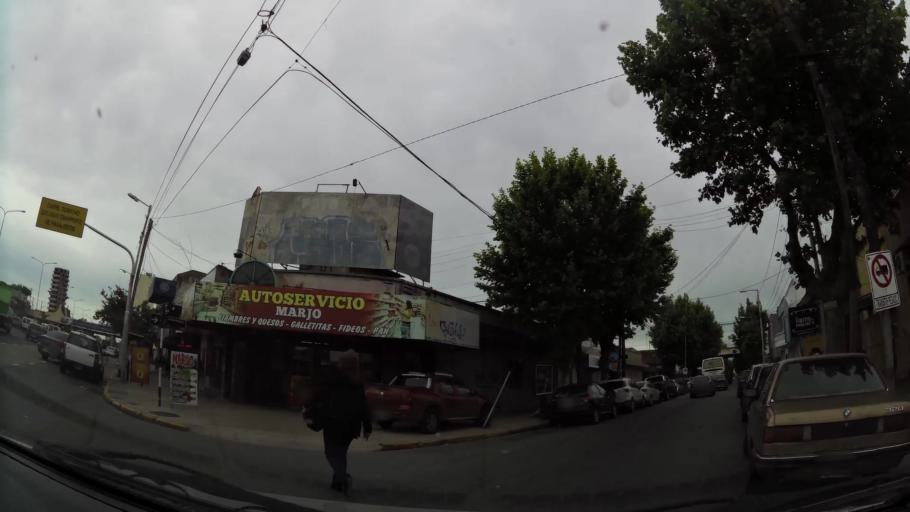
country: AR
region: Buenos Aires
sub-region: Partido de Avellaneda
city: Avellaneda
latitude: -34.6772
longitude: -58.3480
